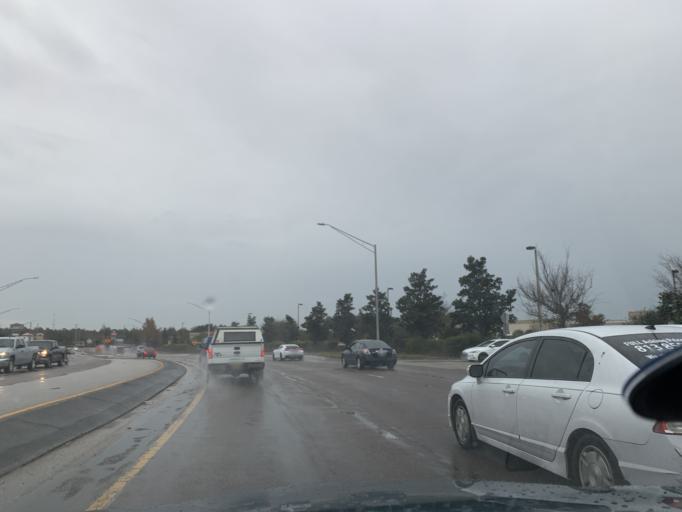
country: US
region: Florida
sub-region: Pasco County
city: Jasmine Estates
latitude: 28.2797
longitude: -82.6759
